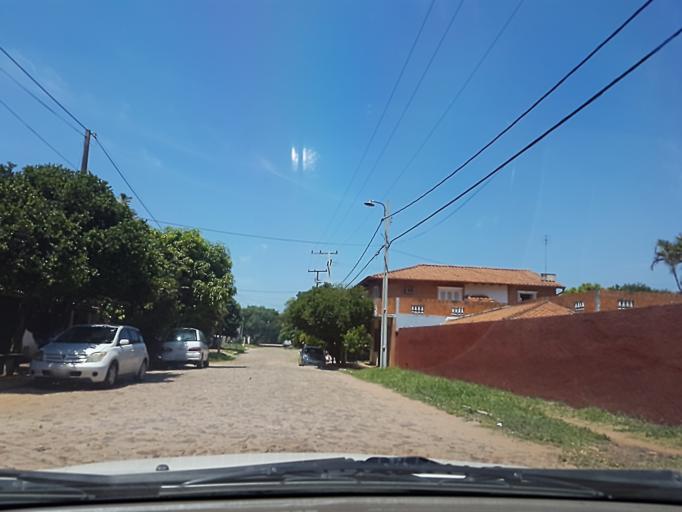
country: PY
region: Central
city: Fernando de la Mora
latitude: -25.2919
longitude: -57.5322
